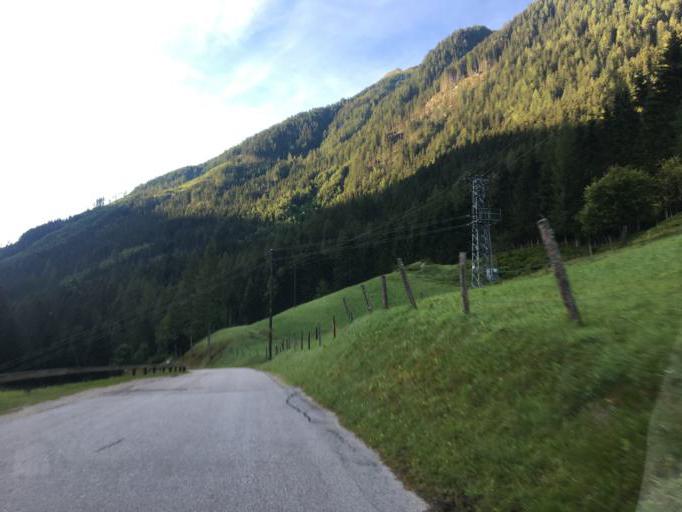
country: AT
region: Styria
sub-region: Politischer Bezirk Liezen
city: Schladming
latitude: 47.3589
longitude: 13.6915
